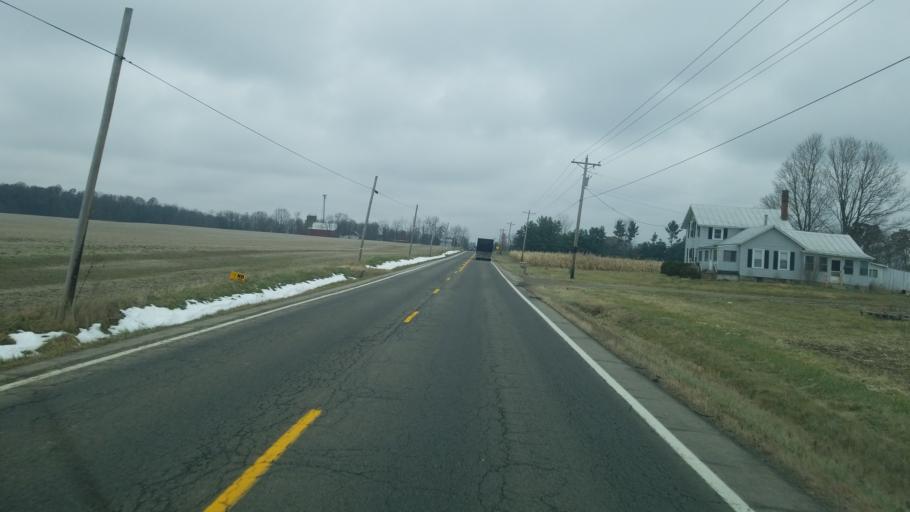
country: US
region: Ohio
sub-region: Huron County
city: Greenwich
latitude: 41.0826
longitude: -82.4873
